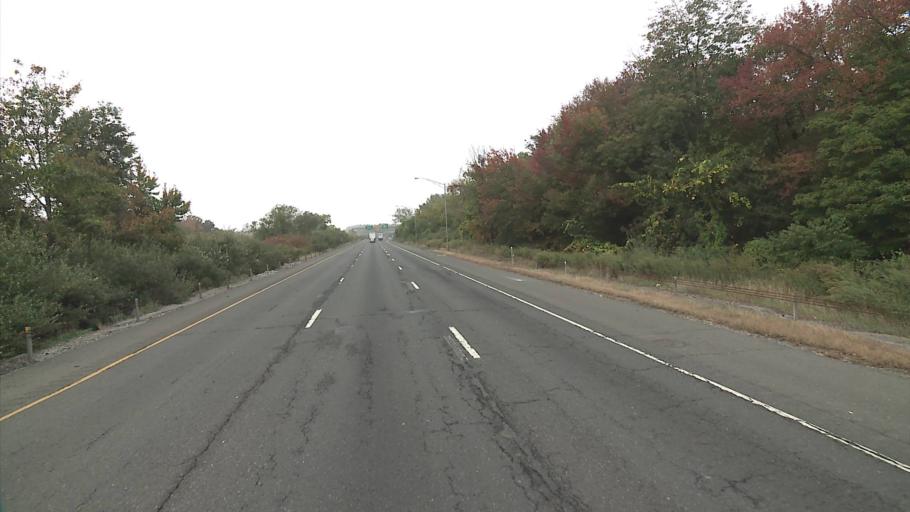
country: US
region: Connecticut
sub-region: Fairfield County
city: Newtown
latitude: 41.4195
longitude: -73.2617
